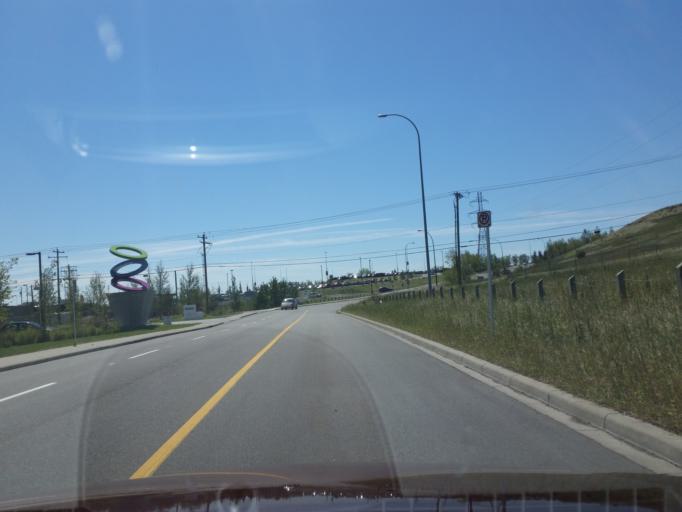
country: CA
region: Alberta
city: Calgary
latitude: 51.0532
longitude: -114.0262
